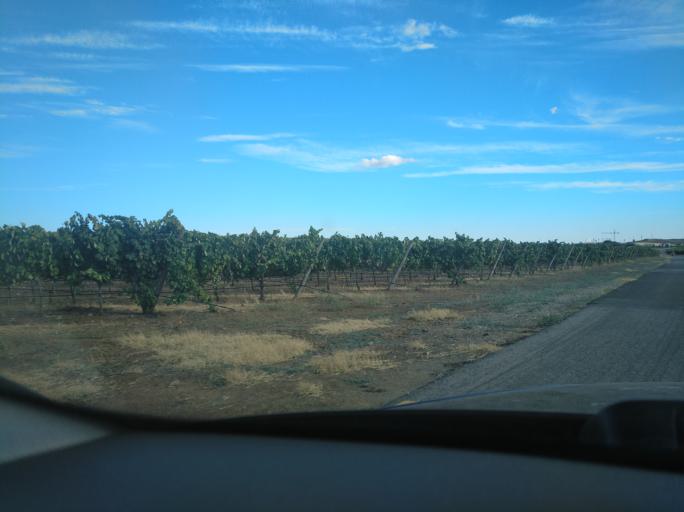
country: PT
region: Portalegre
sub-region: Campo Maior
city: Campo Maior
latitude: 39.0510
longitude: -7.0977
